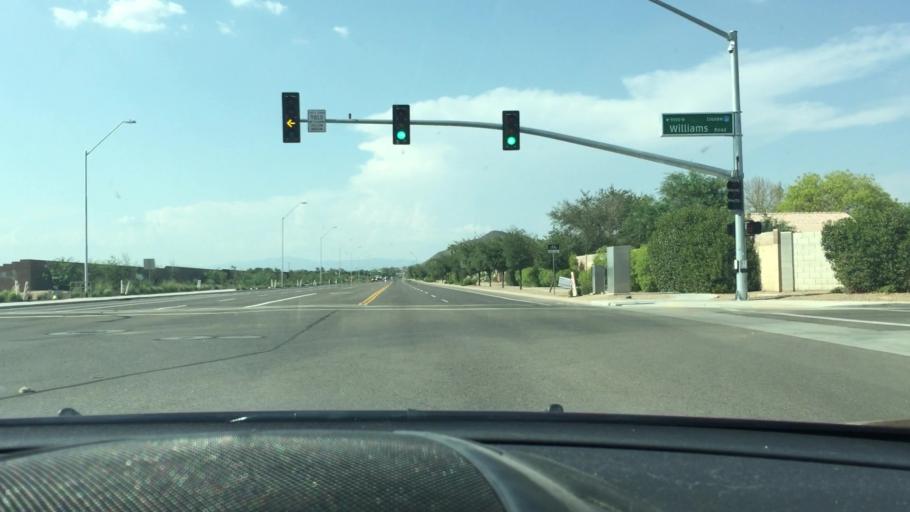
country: US
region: Arizona
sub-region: Maricopa County
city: Sun City West
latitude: 33.6890
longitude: -112.2551
